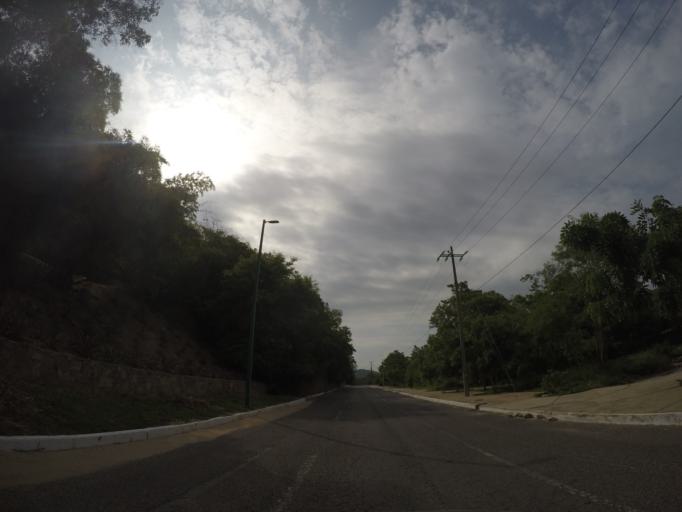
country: MX
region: Oaxaca
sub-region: Santa Maria Huatulco
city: Sector H Tres
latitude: 15.7747
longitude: -96.1479
